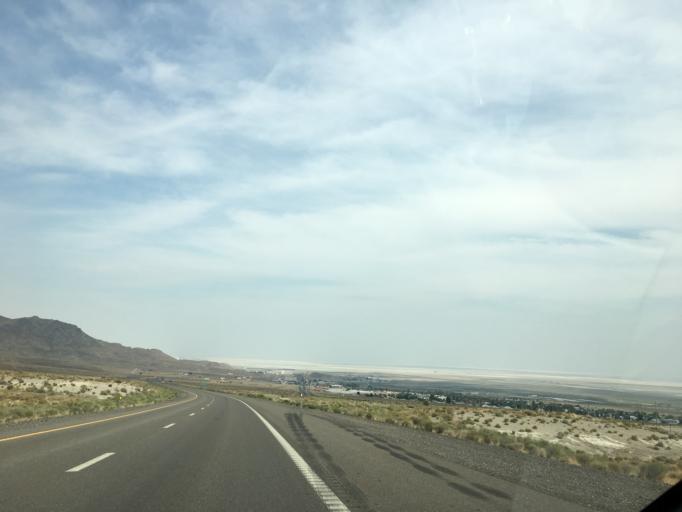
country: US
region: Nevada
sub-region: Elko County
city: West Wendover
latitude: 40.7443
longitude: -114.0964
